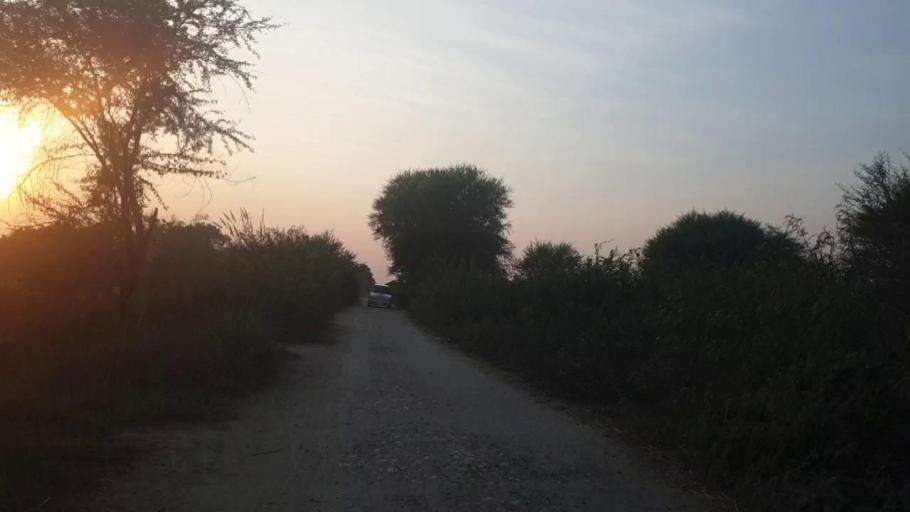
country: PK
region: Sindh
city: Tando Jam
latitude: 25.3831
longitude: 68.5748
